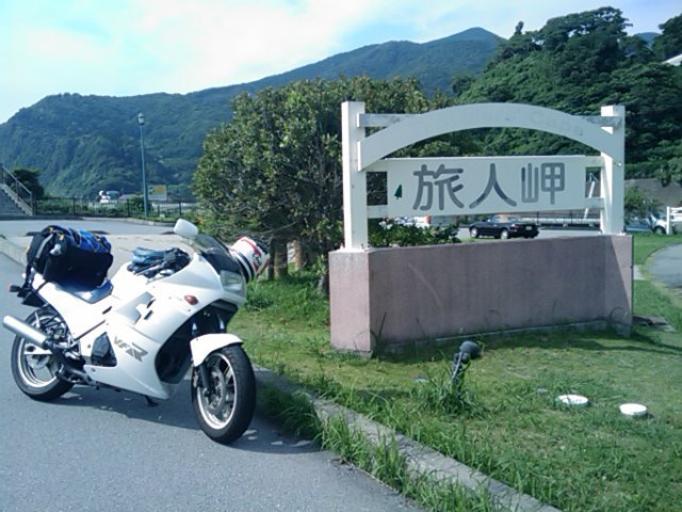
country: JP
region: Shizuoka
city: Heda
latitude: 34.9167
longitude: 138.7858
